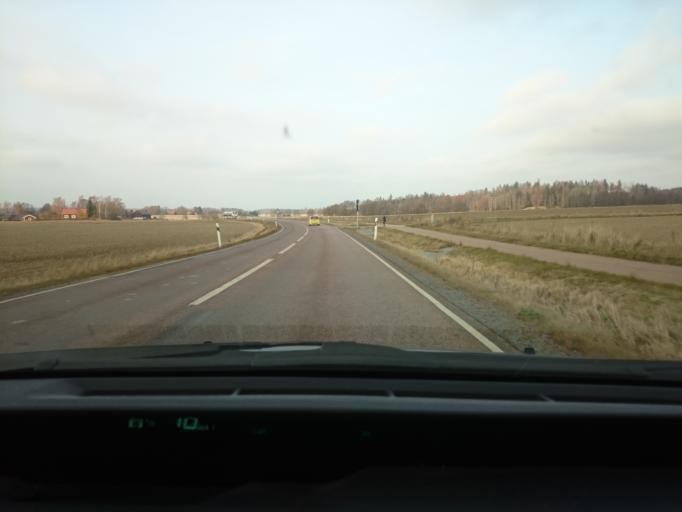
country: SE
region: Vaestmanland
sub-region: Vasteras
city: Skultuna
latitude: 59.6830
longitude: 16.4617
